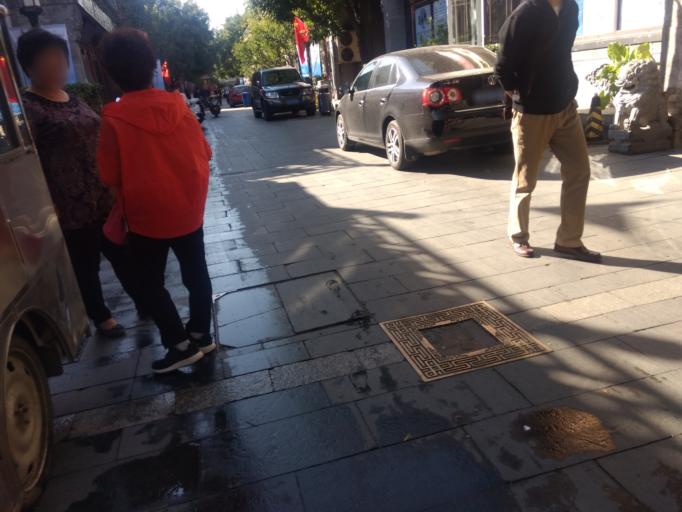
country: CN
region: Beijing
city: Beijing
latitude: 39.8938
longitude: 116.3801
